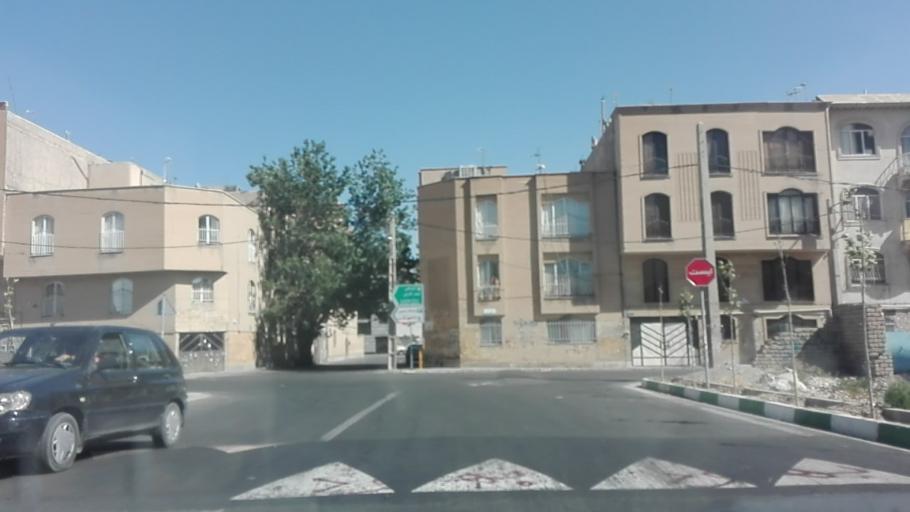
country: IR
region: Tehran
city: Shahriar
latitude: 35.6479
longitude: 51.0601
